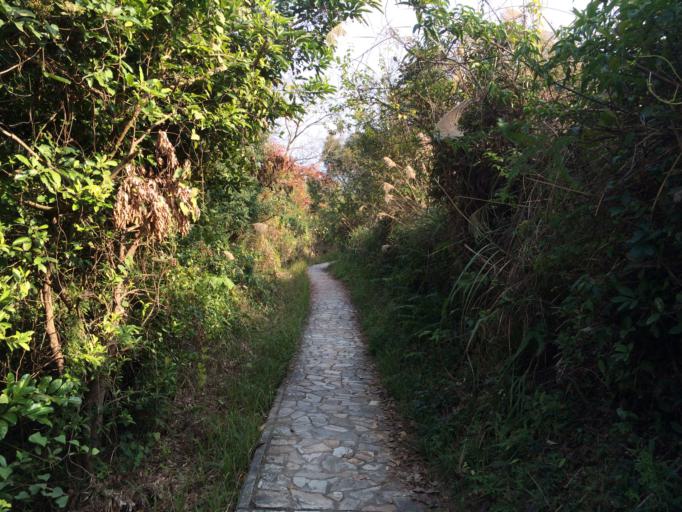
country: HK
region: Tai Po
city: Tai Po
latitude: 22.4514
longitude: 114.2155
